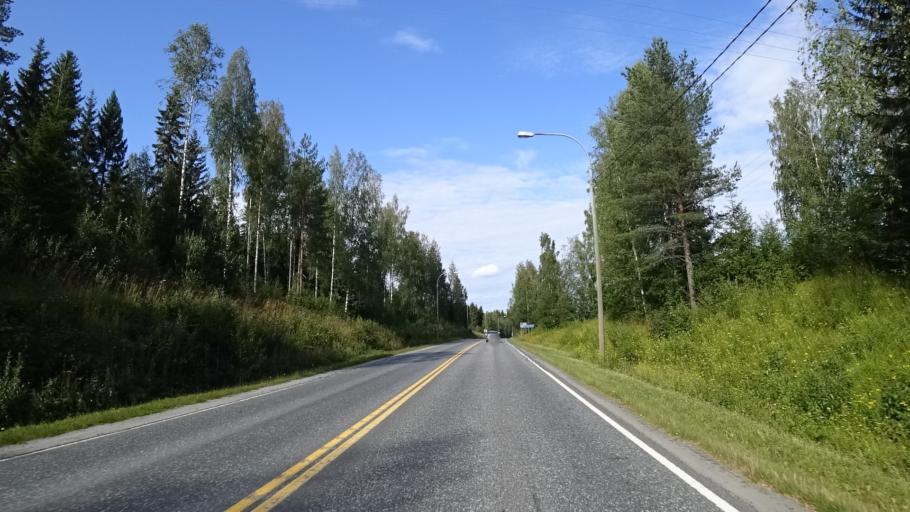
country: FI
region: North Karelia
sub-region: Joensuu
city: Eno
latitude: 62.7882
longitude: 30.0810
